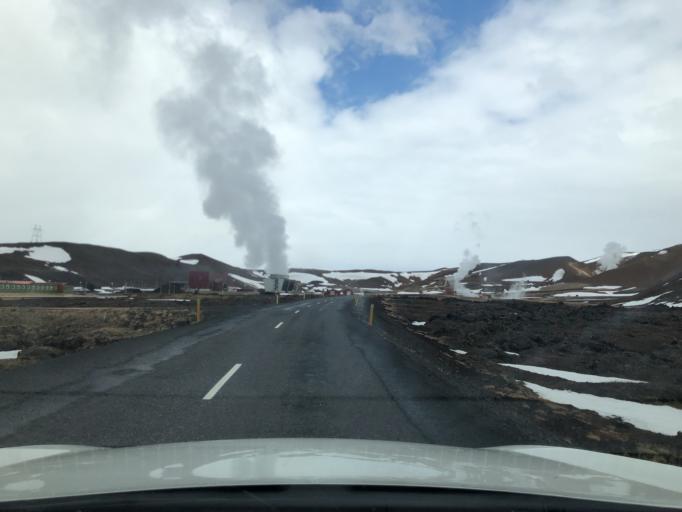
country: IS
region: Northeast
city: Laugar
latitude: 65.6971
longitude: -16.7739
